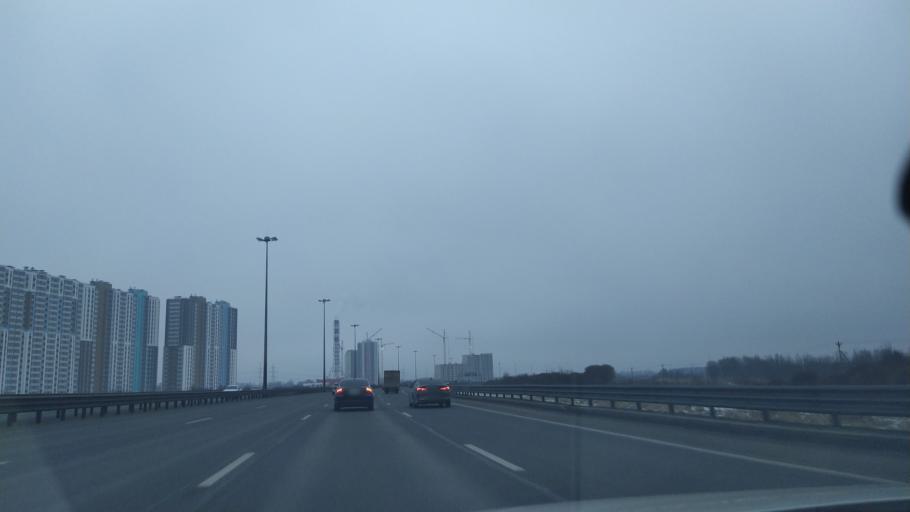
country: RU
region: St.-Petersburg
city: Krasnogvargeisky
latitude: 60.0121
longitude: 30.4723
